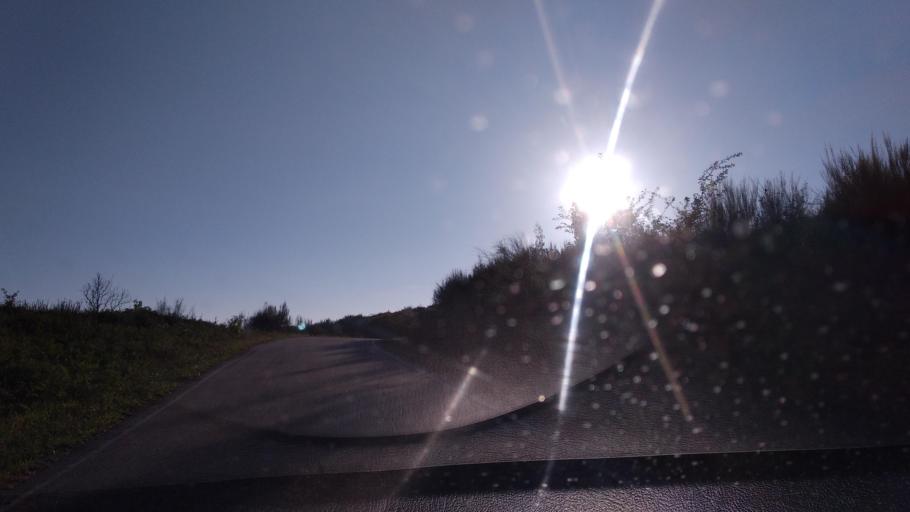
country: ES
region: Galicia
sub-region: Provincia de Pontevedra
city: Ponte Caldelas
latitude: 42.3570
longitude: -8.4964
